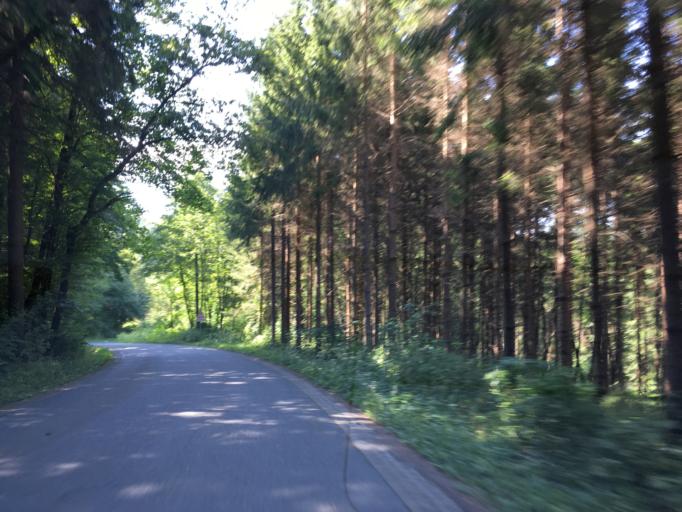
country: AT
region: Styria
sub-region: Politischer Bezirk Leibnitz
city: Sankt Nikolai im Sausal
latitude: 46.8086
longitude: 15.4574
